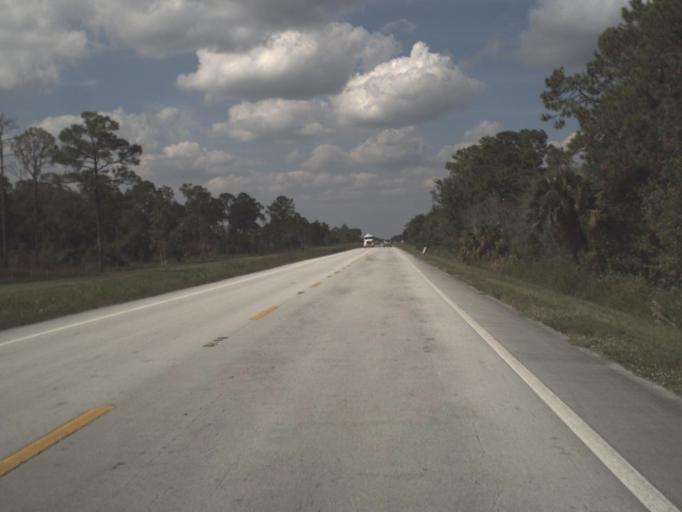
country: US
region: Florida
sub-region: Indian River County
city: Fellsmere
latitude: 27.5868
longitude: -80.8394
